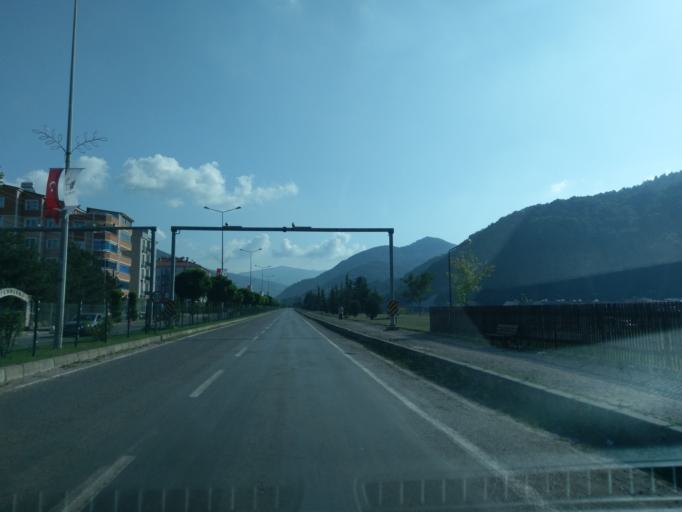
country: TR
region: Sinop
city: Ayancik
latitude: 41.9307
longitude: 34.5848
